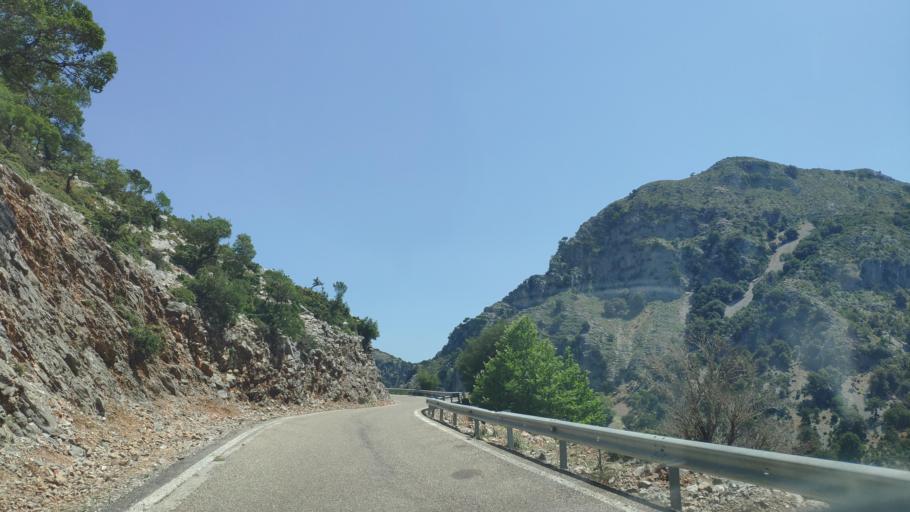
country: GR
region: West Greece
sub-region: Nomos Aitolias kai Akarnanias
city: Krikellos
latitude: 39.0065
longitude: 21.3706
